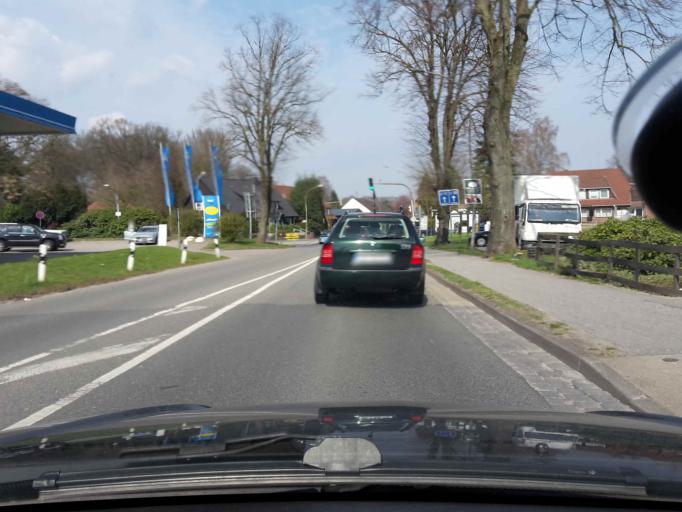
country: DE
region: Lower Saxony
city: Seevetal
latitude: 53.3823
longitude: 9.9798
